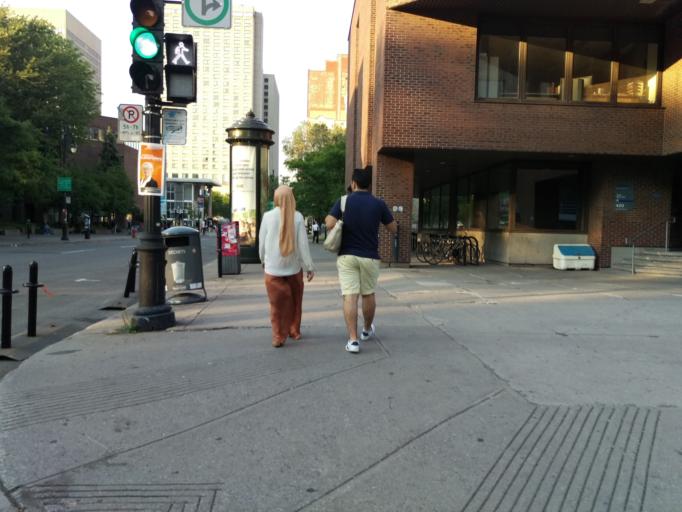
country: CA
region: Quebec
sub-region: Montreal
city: Montreal
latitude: 45.5137
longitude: -73.5605
